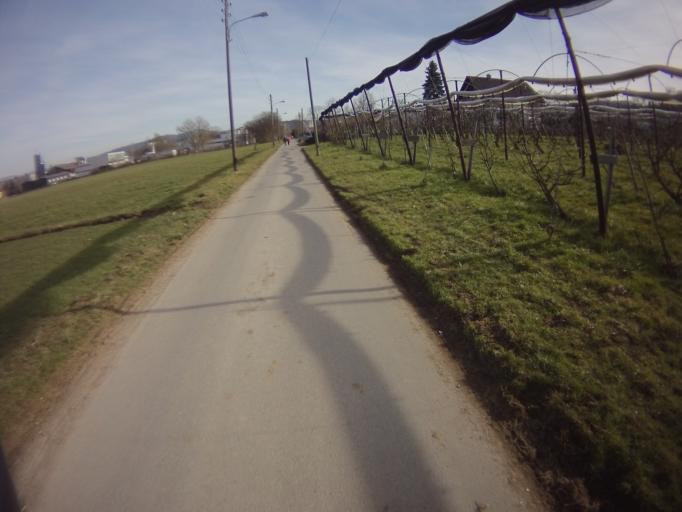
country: CH
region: Zurich
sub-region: Bezirk Dietikon
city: Dietikon / Almend
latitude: 47.4098
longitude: 8.3829
